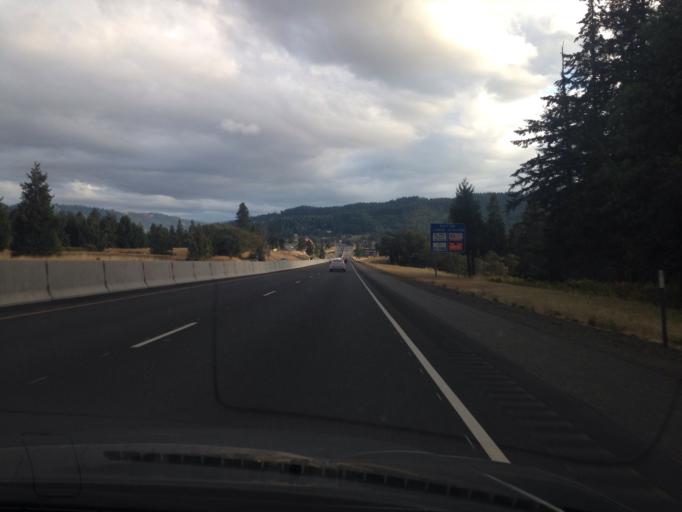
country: US
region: Oregon
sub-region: Douglas County
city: Sutherlin
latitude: 43.3964
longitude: -123.3366
